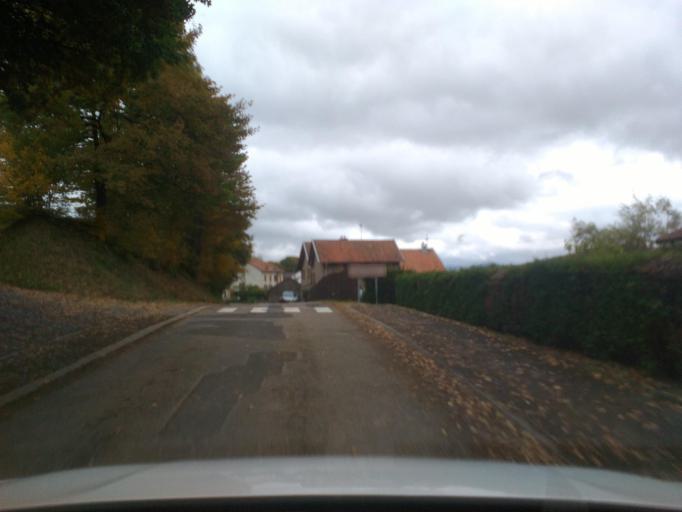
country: FR
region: Lorraine
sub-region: Departement des Vosges
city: Moyenmoutier
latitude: 48.3825
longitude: 6.9289
